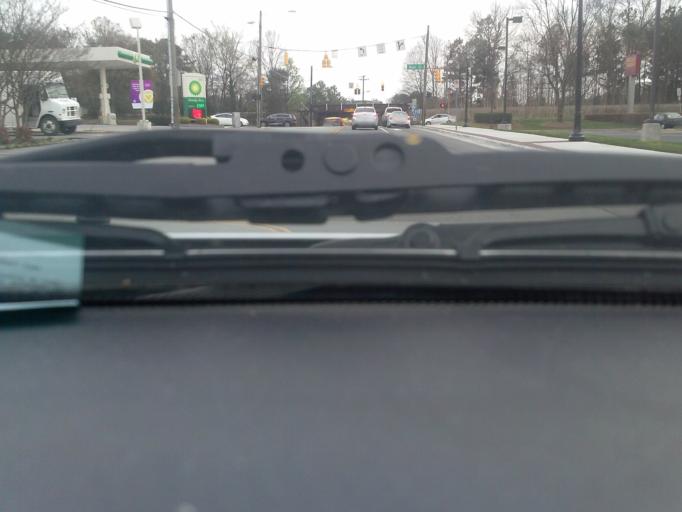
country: US
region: North Carolina
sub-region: Durham County
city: Durham
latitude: 36.0073
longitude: -78.9222
